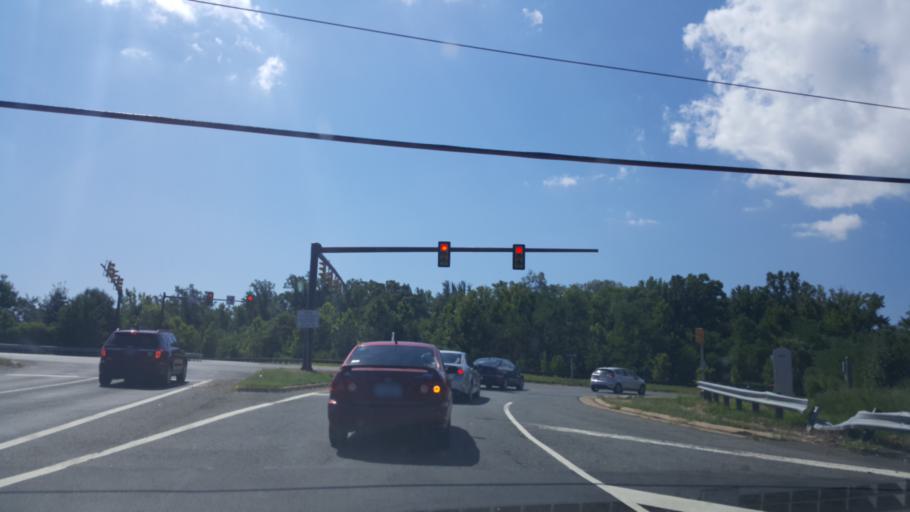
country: US
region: Virginia
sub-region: Fairfax County
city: Newington
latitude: 38.7241
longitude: -77.1845
